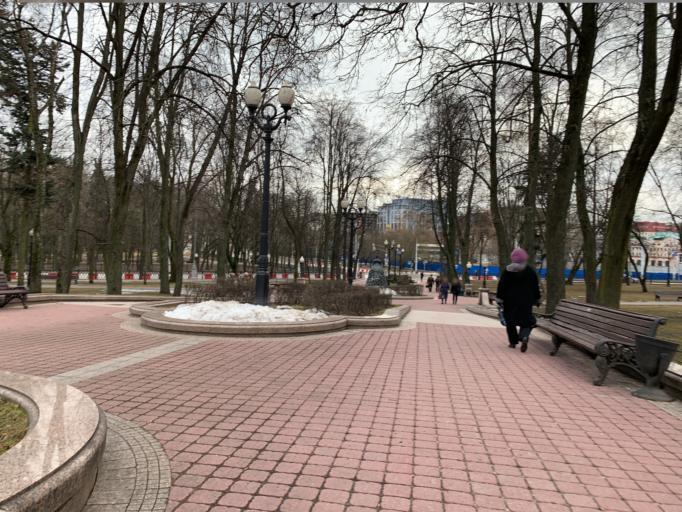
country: BY
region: Minsk
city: Minsk
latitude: 53.9092
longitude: 27.5612
